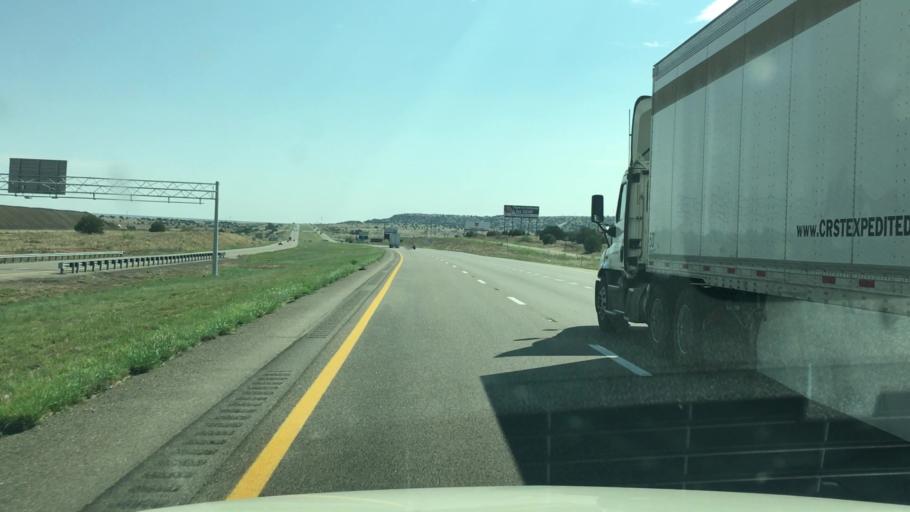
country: US
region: New Mexico
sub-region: Guadalupe County
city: Santa Rosa
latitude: 34.9487
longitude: -104.6380
